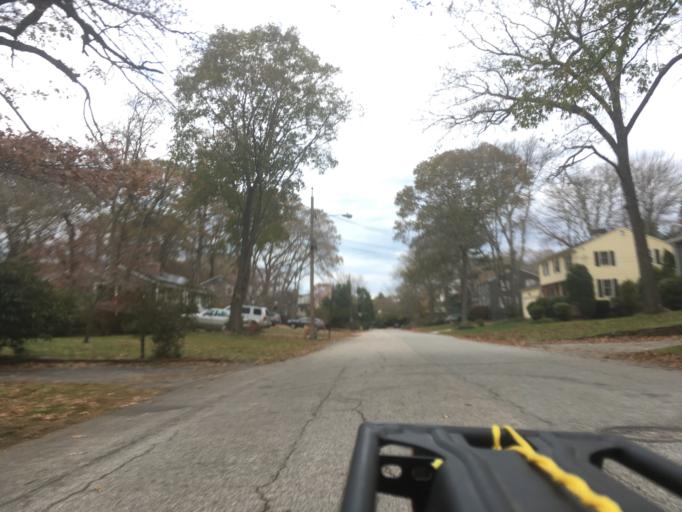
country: US
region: Rhode Island
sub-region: Kent County
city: East Greenwich
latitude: 41.6483
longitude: -71.4683
